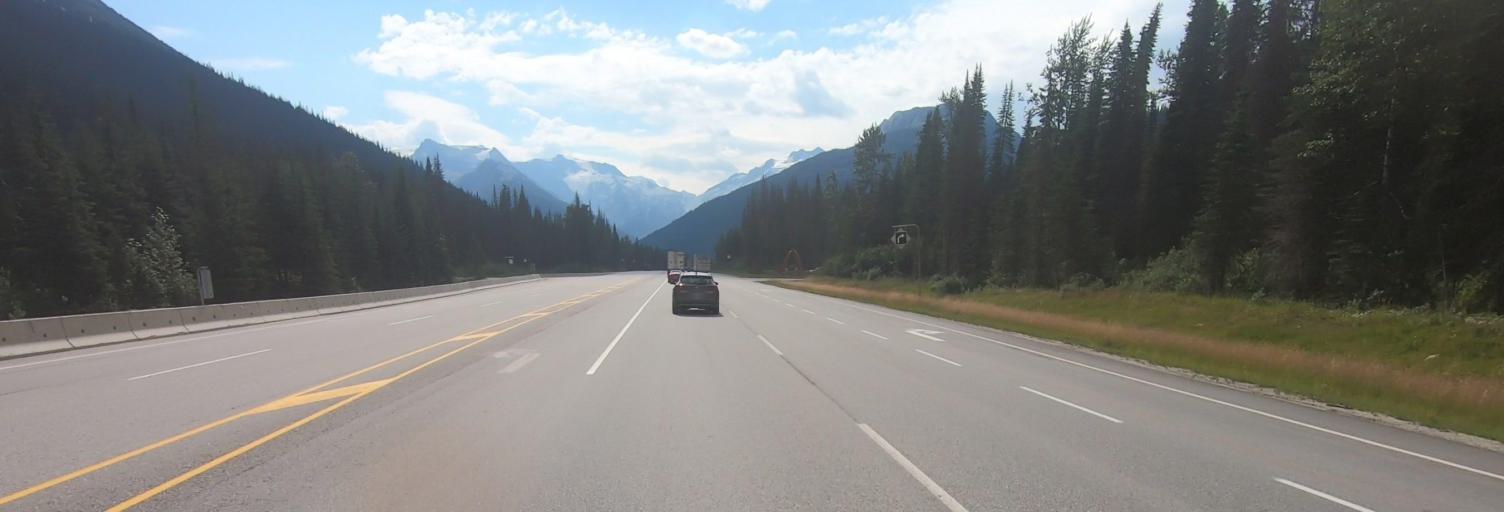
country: CA
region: British Columbia
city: Golden
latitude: 51.2915
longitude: -117.5160
